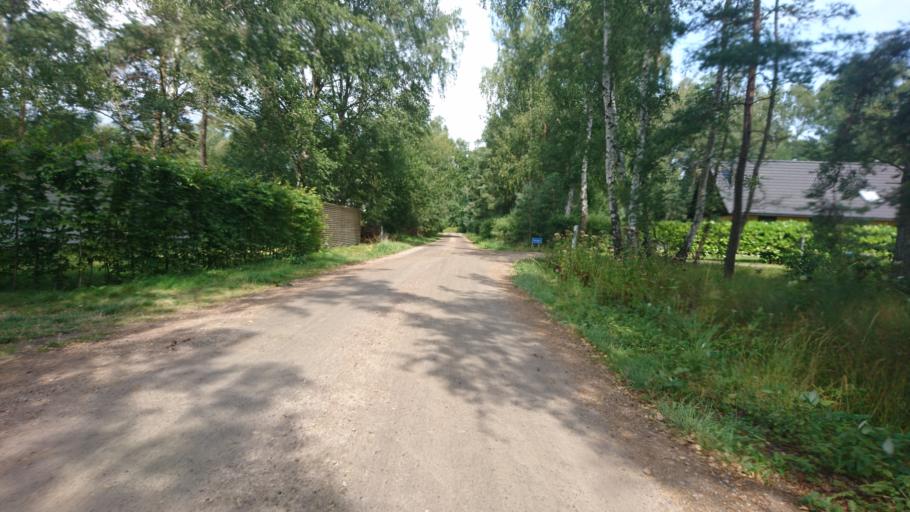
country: SE
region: Skane
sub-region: Vellinge Kommun
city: Ljunghusen
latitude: 55.4039
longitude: 12.9098
